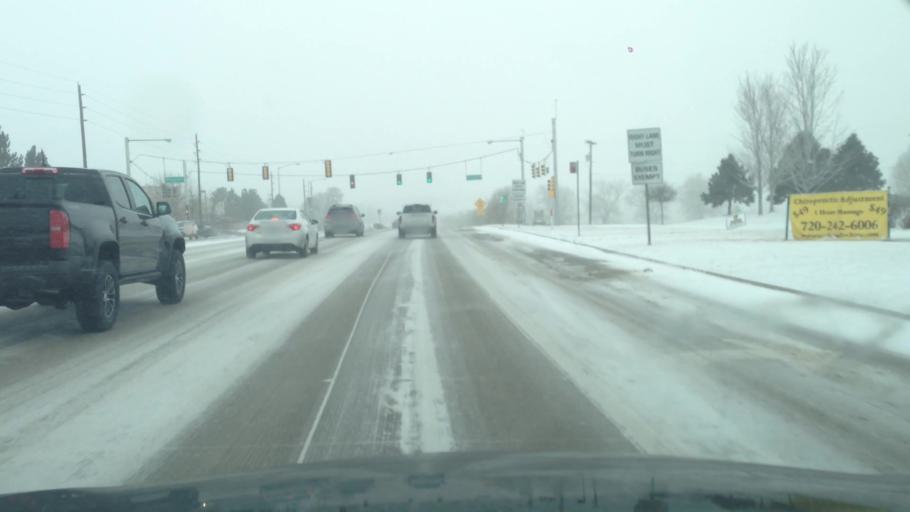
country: US
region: Colorado
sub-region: Arapahoe County
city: Dove Valley
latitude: 39.6249
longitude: -104.8221
